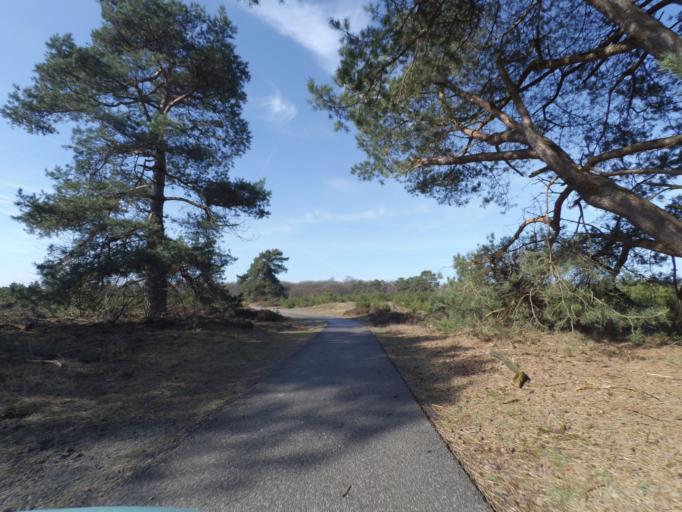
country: NL
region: Gelderland
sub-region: Gemeente Apeldoorn
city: Uddel
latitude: 52.2037
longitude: 5.7658
